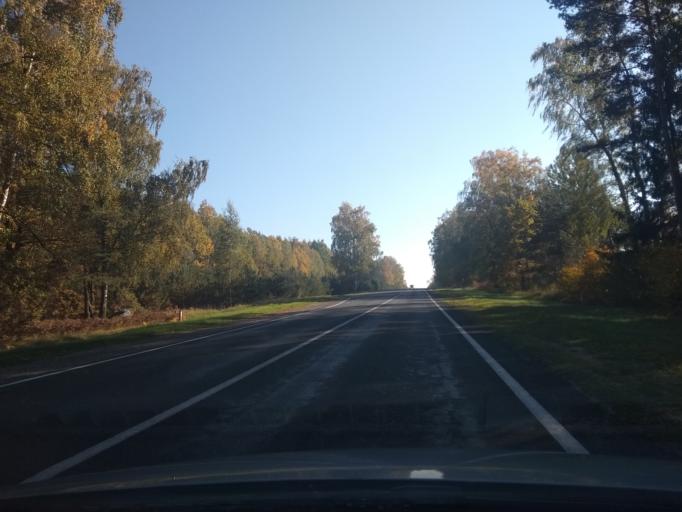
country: BY
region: Grodnenskaya
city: Zel'va
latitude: 53.1408
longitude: 24.9023
